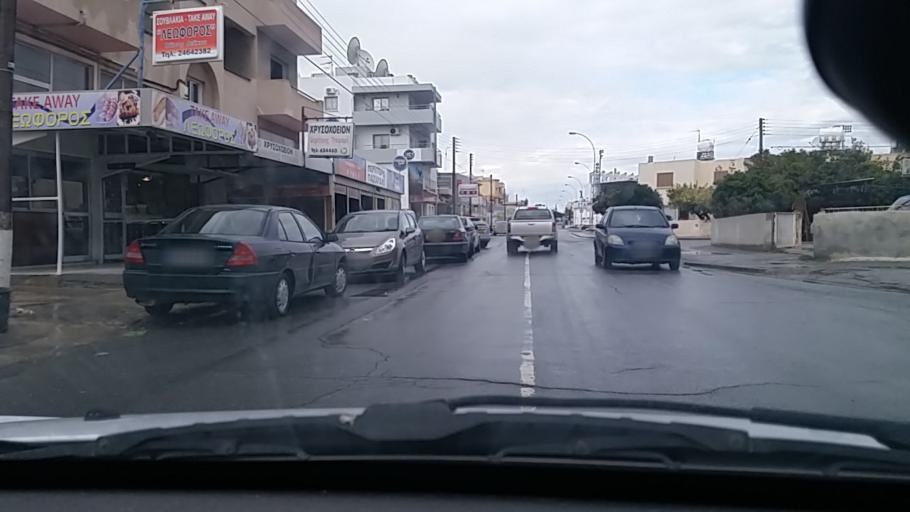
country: CY
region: Larnaka
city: Larnaca
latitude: 34.9343
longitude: 33.6217
